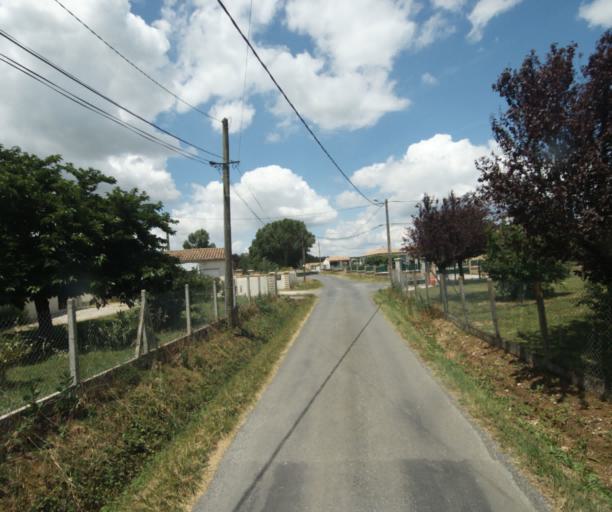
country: FR
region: Midi-Pyrenees
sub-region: Departement du Tarn
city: Soual
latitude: 43.5411
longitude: 2.0617
